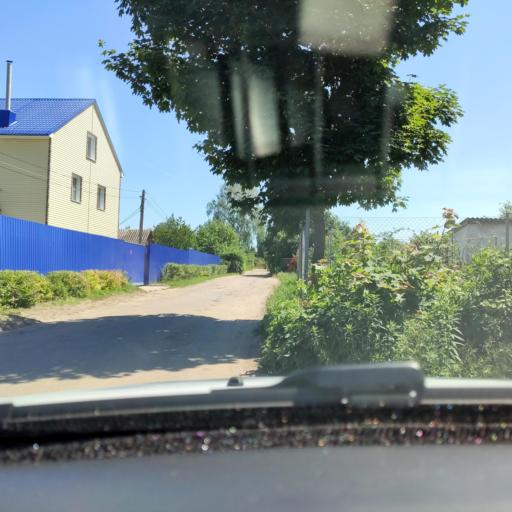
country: RU
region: Voronezj
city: Shilovo
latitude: 51.5927
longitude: 39.1456
